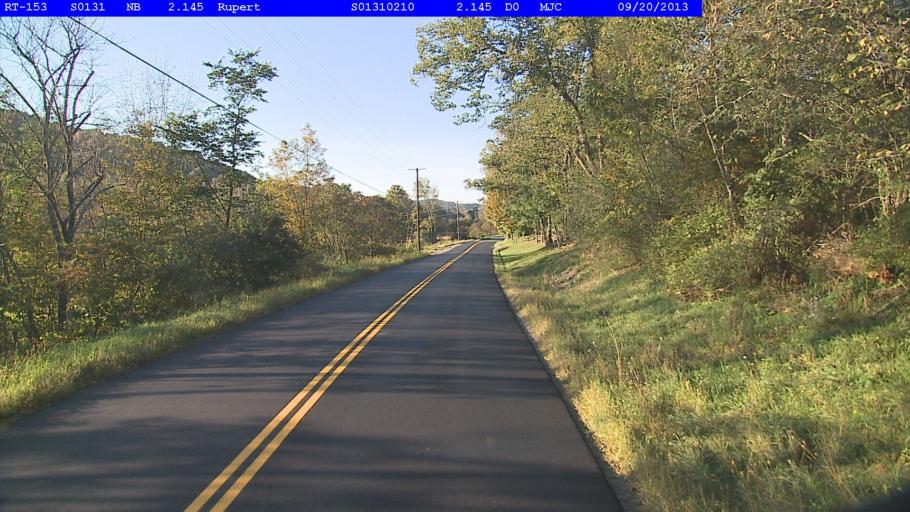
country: US
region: New York
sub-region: Washington County
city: Granville
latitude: 43.2859
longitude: -73.2388
